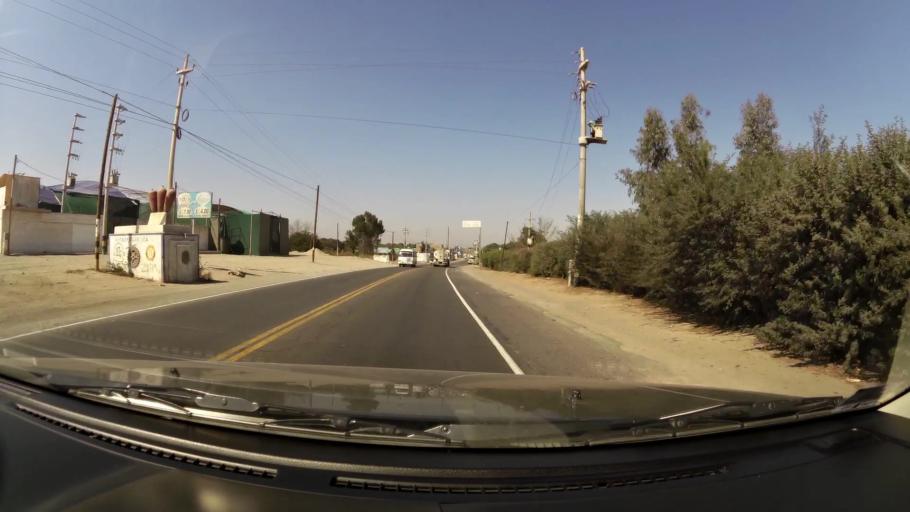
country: PE
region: Ica
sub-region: Provincia de Ica
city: Guadalupe
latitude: -13.9795
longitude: -75.7747
